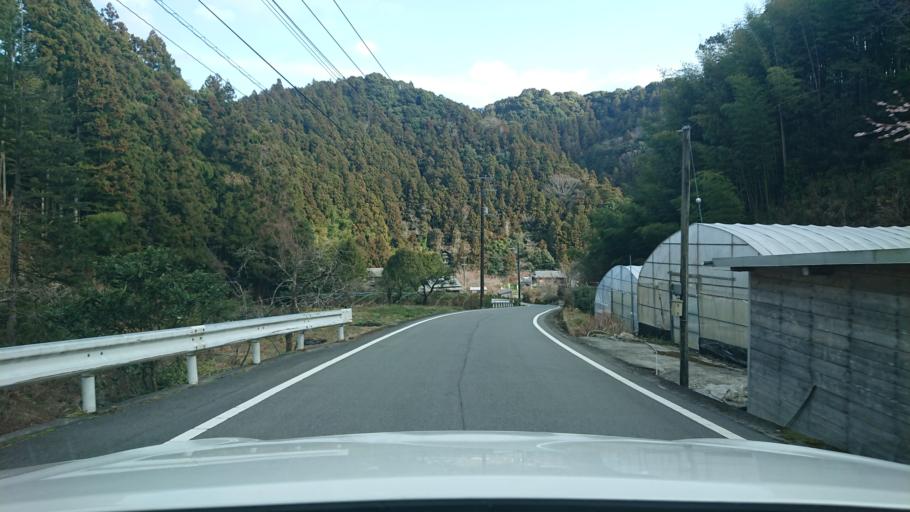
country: JP
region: Tokushima
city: Ishii
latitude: 33.9139
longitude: 134.4159
